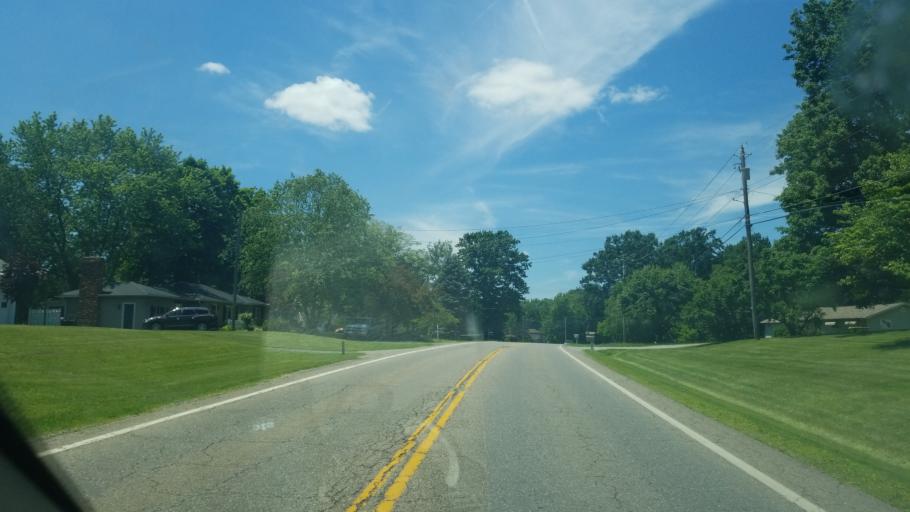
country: US
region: Ohio
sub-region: Columbiana County
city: Salem
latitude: 40.8791
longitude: -80.8610
